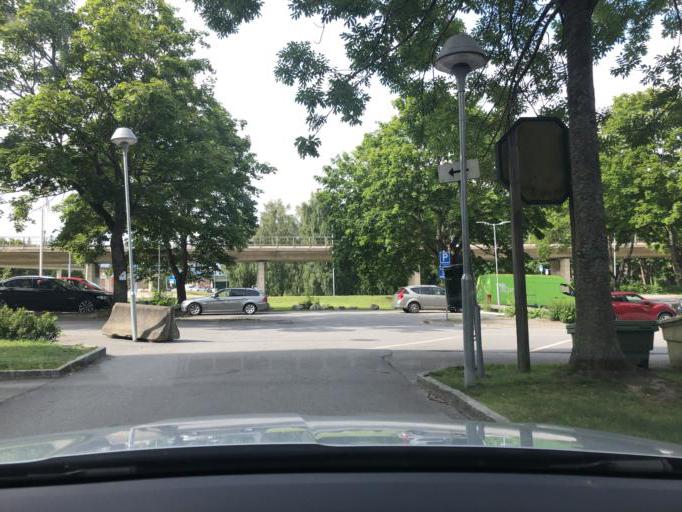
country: SE
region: Stockholm
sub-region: Botkyrka Kommun
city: Fittja
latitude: 59.2486
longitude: 17.8662
